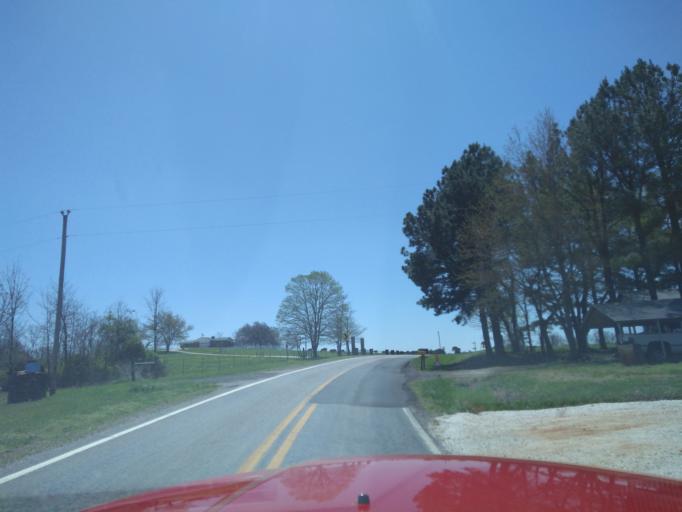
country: US
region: Arkansas
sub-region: Washington County
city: West Fork
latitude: 35.8380
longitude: -94.2679
